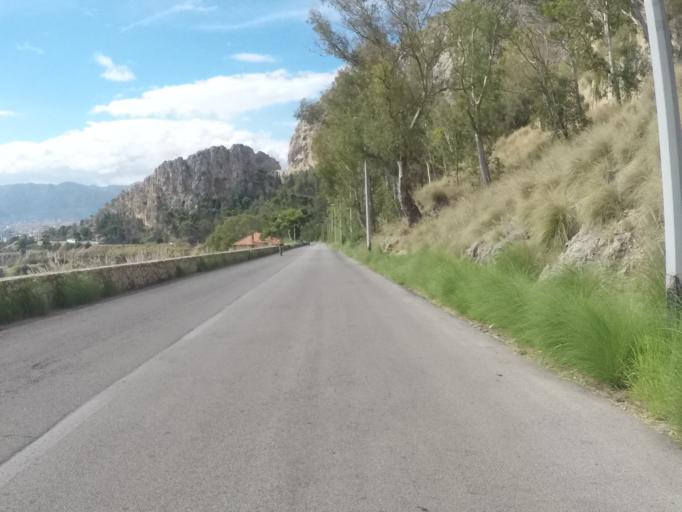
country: IT
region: Sicily
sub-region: Palermo
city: Palermo
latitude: 38.1562
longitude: 13.3673
